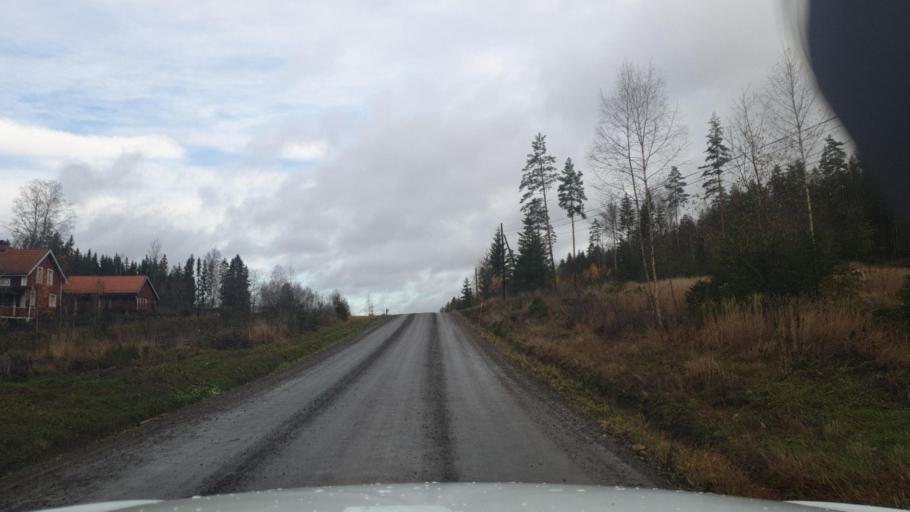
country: NO
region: Ostfold
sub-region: Romskog
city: Romskog
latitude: 59.8420
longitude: 11.9816
